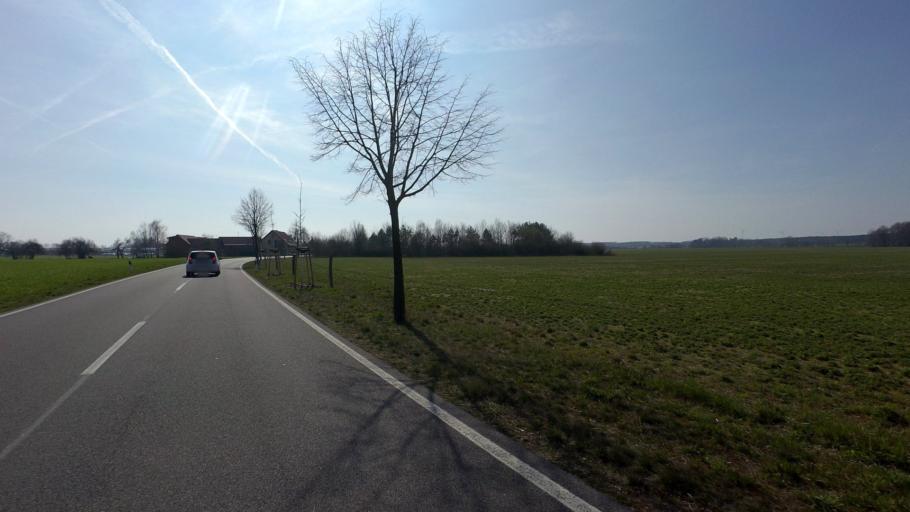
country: DE
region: Brandenburg
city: Golssen
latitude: 51.9452
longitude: 13.5989
